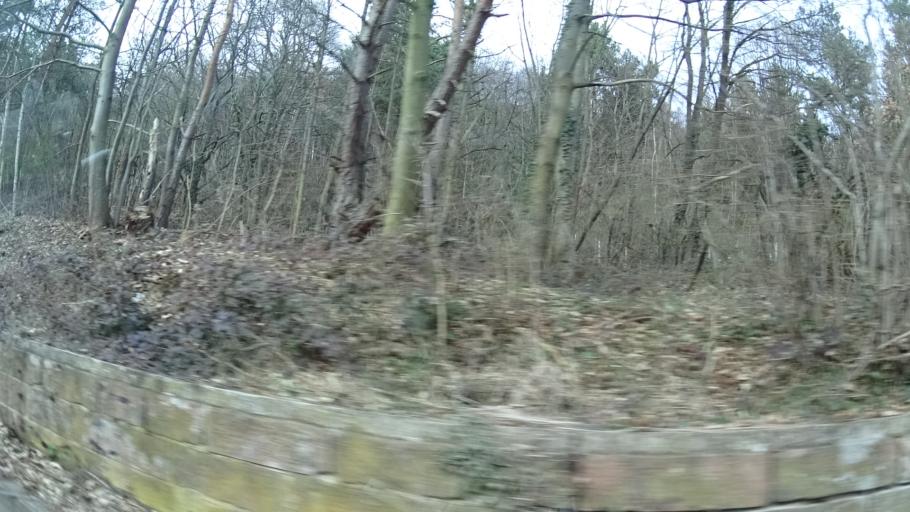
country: DE
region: Rheinland-Pfalz
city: Sankt Martin
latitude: 49.3014
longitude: 8.0919
